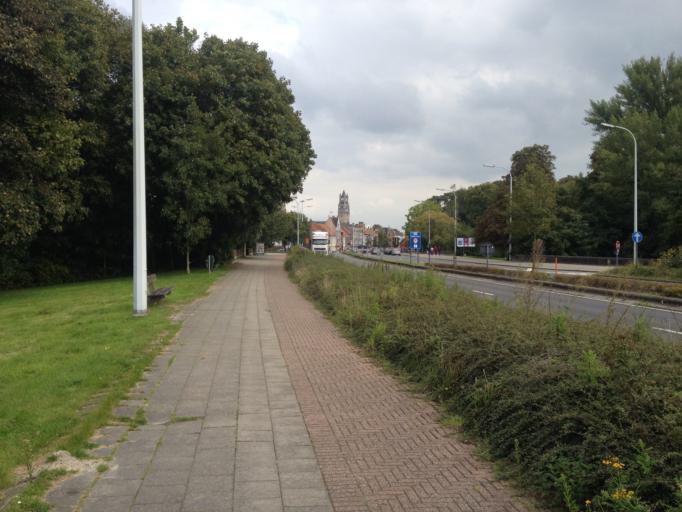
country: BE
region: Flanders
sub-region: Provincie West-Vlaanderen
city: Brugge
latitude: 51.2107
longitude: 3.2118
